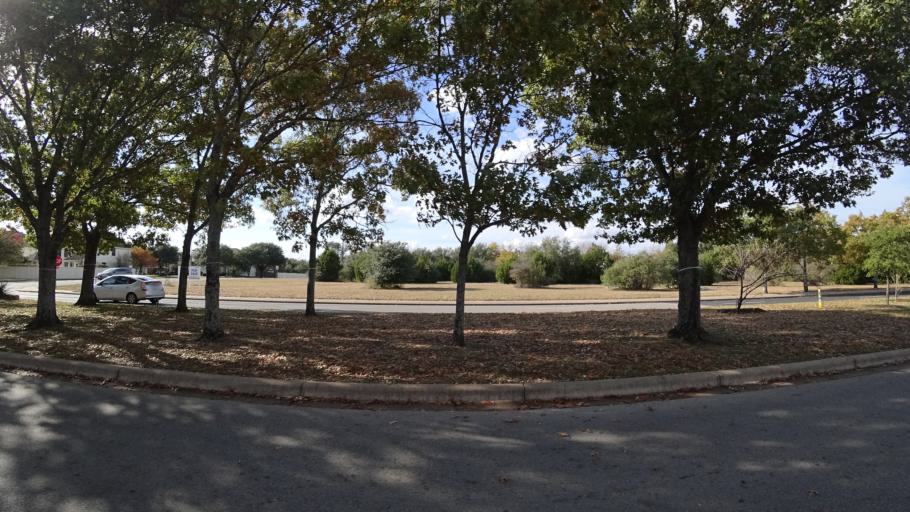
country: US
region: Texas
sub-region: Williamson County
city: Brushy Creek
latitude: 30.5062
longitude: -97.7380
